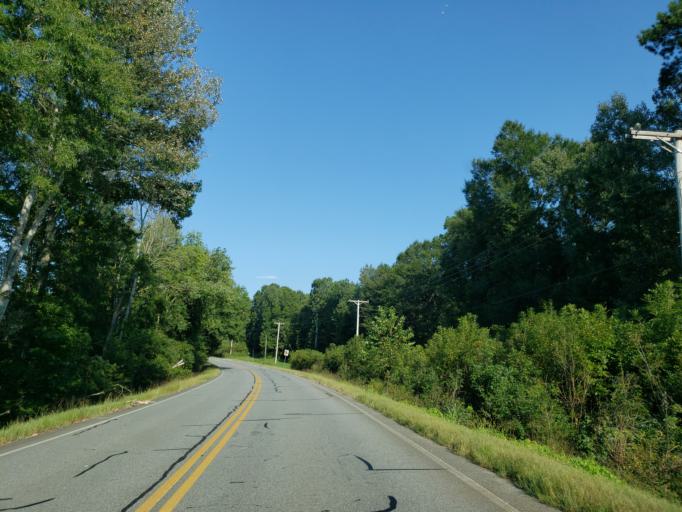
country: US
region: Georgia
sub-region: Whitfield County
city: Varnell
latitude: 34.9215
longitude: -84.8323
